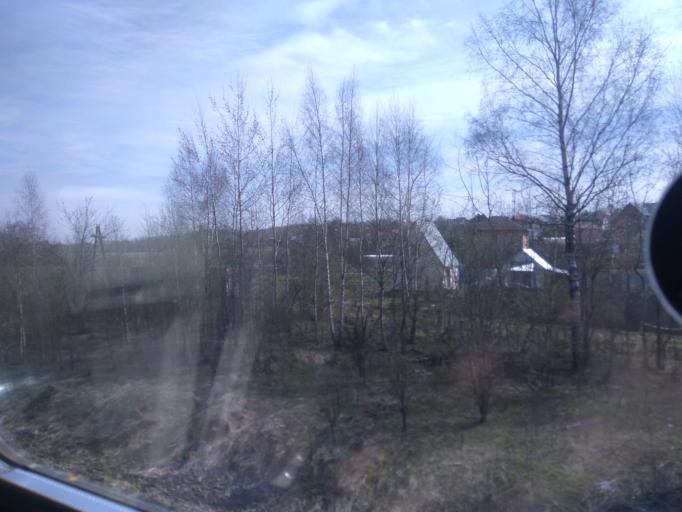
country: RU
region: Moskovskaya
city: Lugovaya
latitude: 56.0658
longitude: 37.4933
